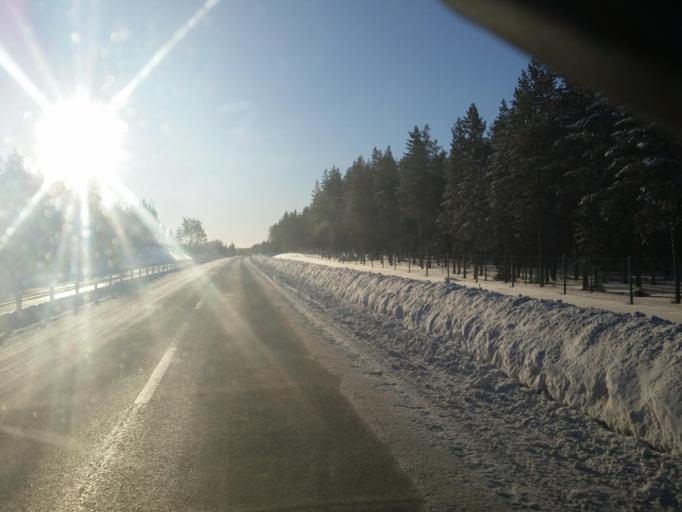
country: SE
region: Norrbotten
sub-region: Pitea Kommun
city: Pitea
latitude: 65.2752
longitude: 21.4516
